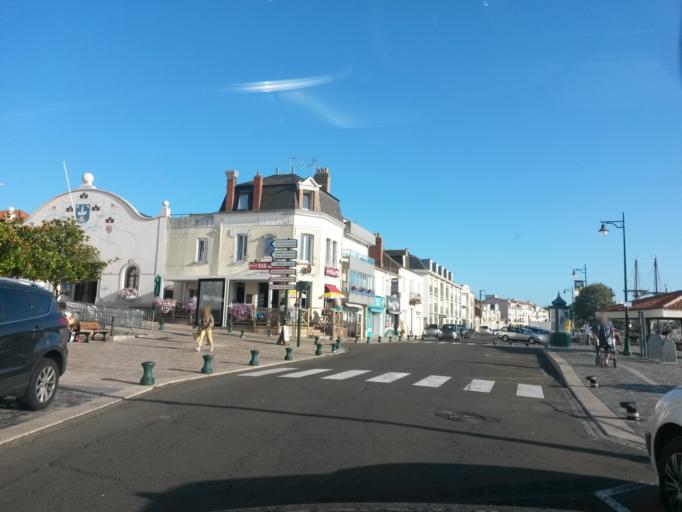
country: FR
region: Pays de la Loire
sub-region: Departement de la Vendee
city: Les Sables-d'Olonne
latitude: 46.4972
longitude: -1.7967
